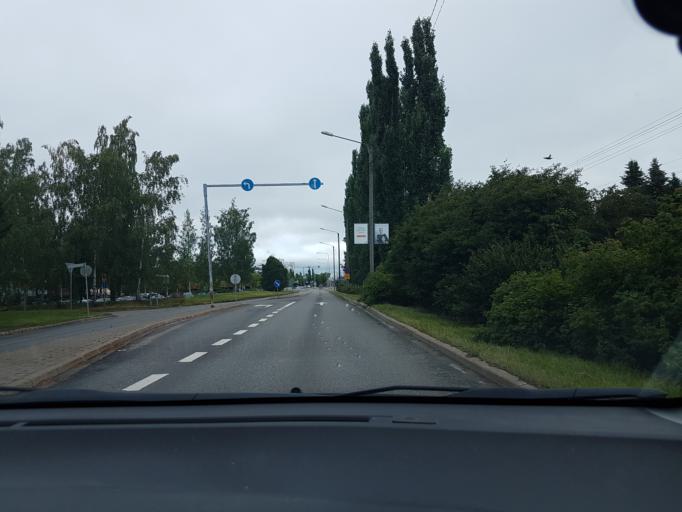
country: FI
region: Uusimaa
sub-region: Helsinki
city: Vantaa
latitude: 60.2726
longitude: 25.0348
